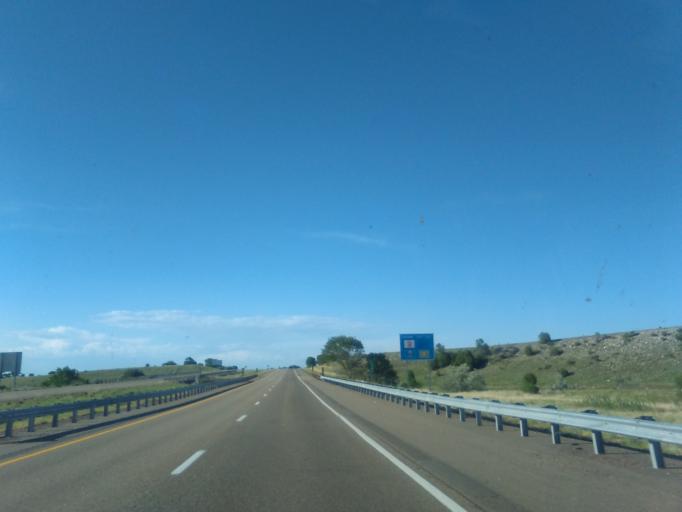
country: US
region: New Mexico
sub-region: San Miguel County
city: Las Vegas
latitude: 35.6089
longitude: -105.2050
